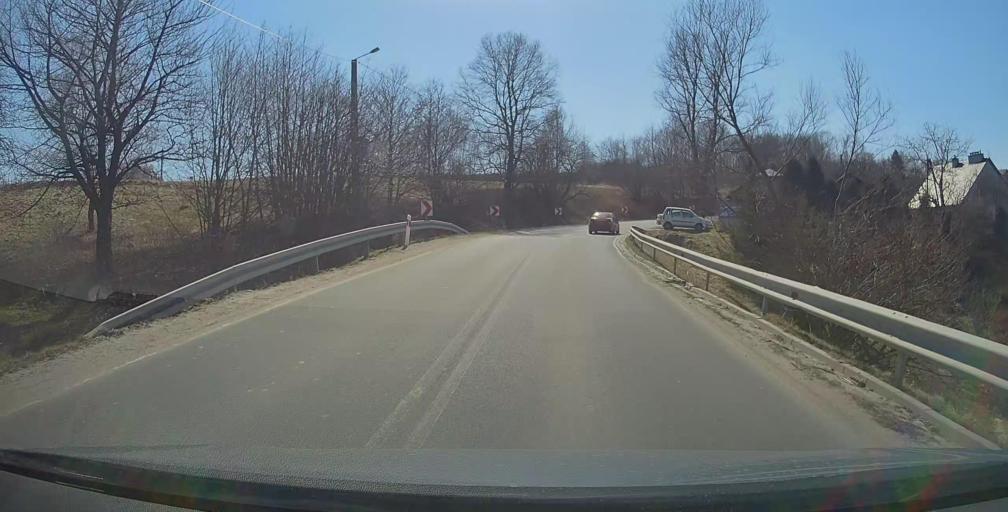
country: PL
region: Subcarpathian Voivodeship
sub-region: Powiat rzeszowski
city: Hyzne
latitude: 49.8976
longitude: 22.2157
